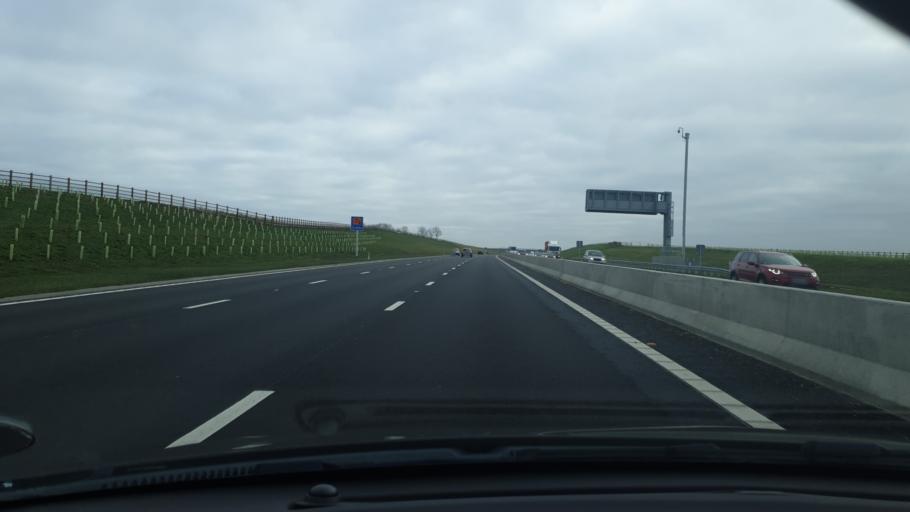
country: GB
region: England
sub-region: Cambridgeshire
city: Brampton
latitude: 52.2988
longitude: -0.1989
